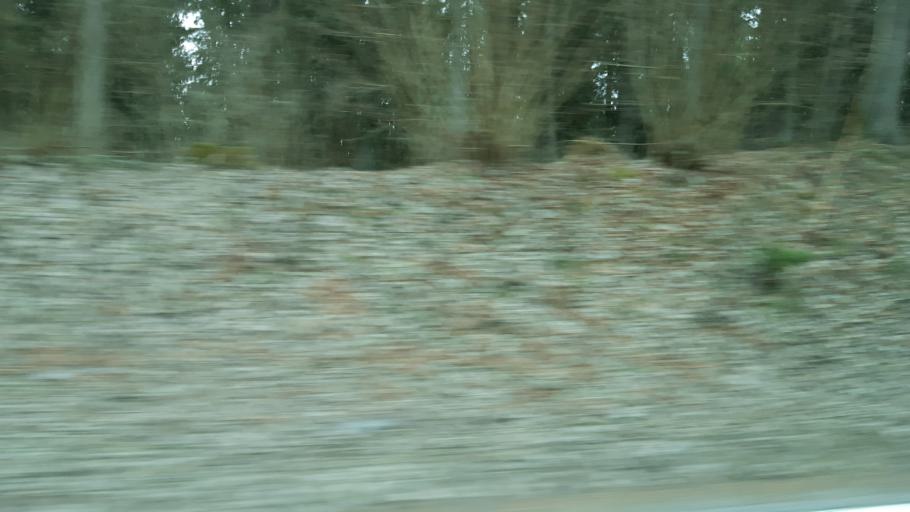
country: PL
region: Podlasie
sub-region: Suwalki
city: Suwalki
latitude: 54.2804
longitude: 22.9463
